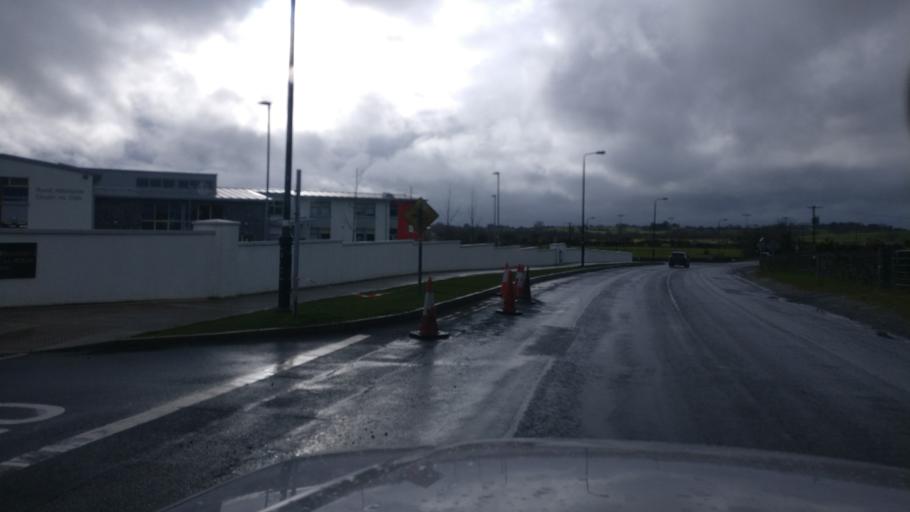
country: IE
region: Leinster
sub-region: An Iarmhi
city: Athlone
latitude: 53.4268
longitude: -8.0213
